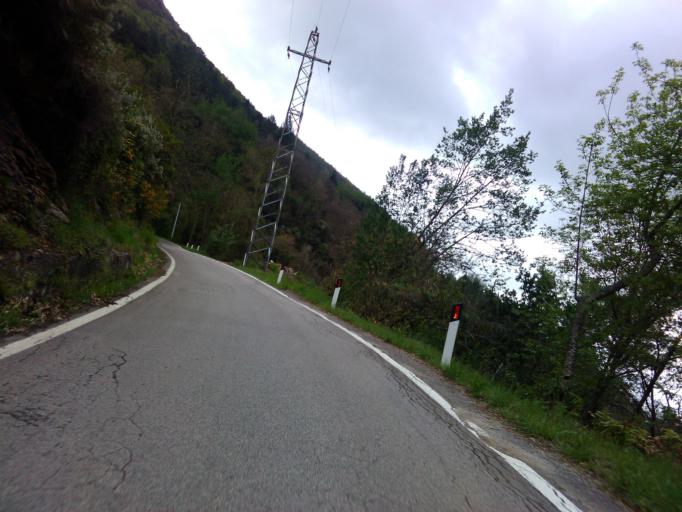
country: IT
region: Tuscany
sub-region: Provincia di Lucca
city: Pontestazzemese
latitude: 43.9703
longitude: 10.2821
